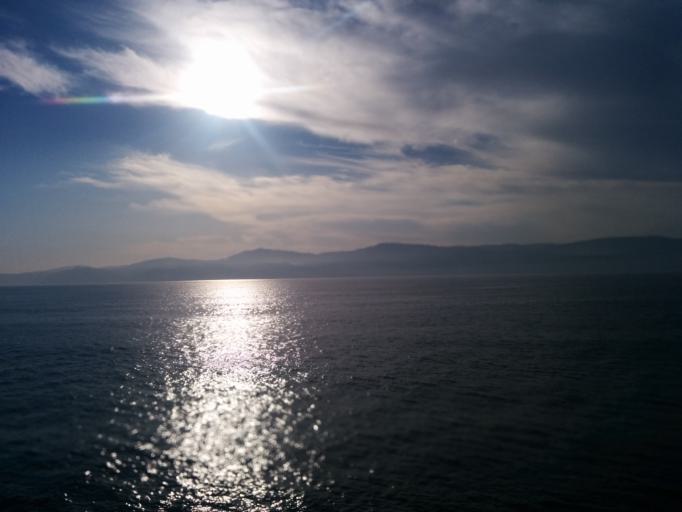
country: MA
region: Tanger-Tetouan
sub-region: Tanger-Assilah
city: Tangier
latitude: 35.8142
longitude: -5.7799
